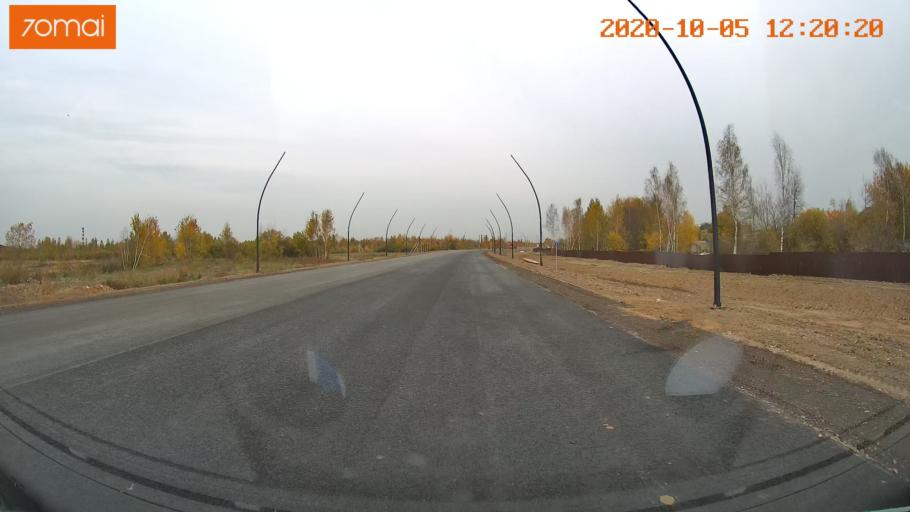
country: RU
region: Ivanovo
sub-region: Gorod Ivanovo
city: Ivanovo
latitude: 56.9624
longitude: 40.9307
